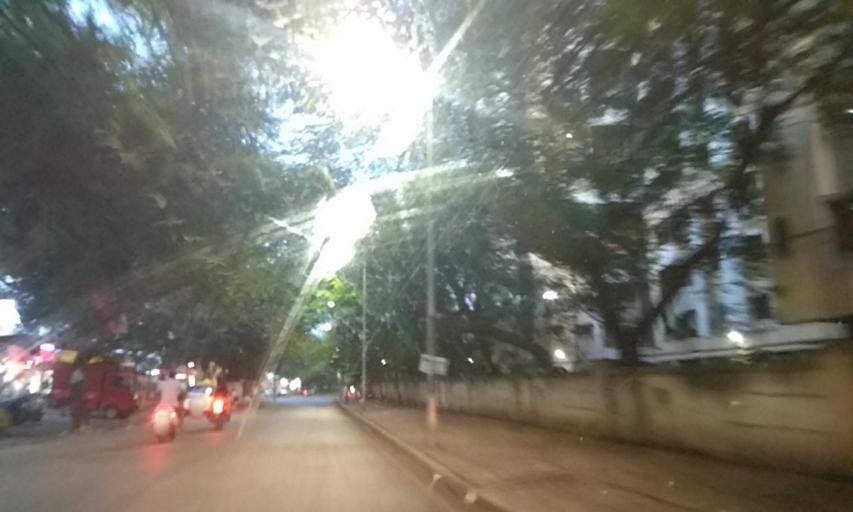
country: IN
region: Maharashtra
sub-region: Pune Division
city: Pune
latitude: 18.5227
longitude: 73.9277
